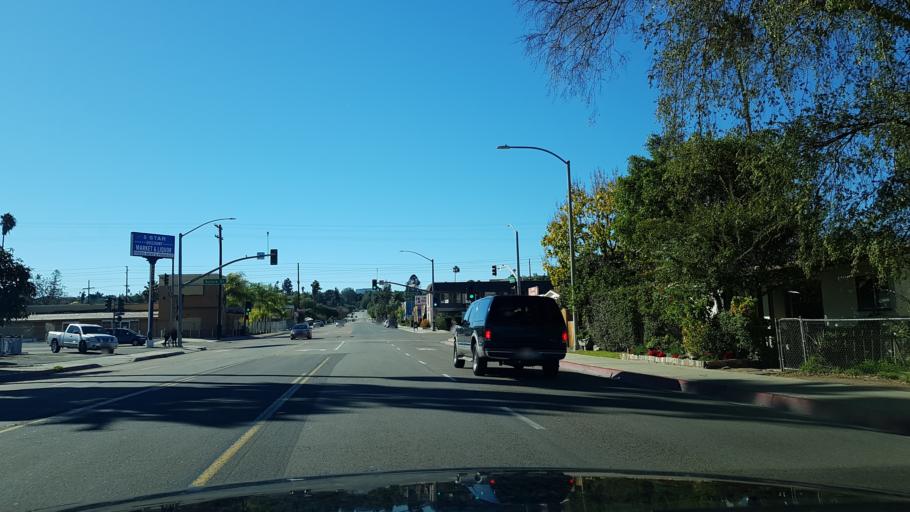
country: US
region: California
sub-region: San Diego County
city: Escondido
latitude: 33.1116
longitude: -117.0824
